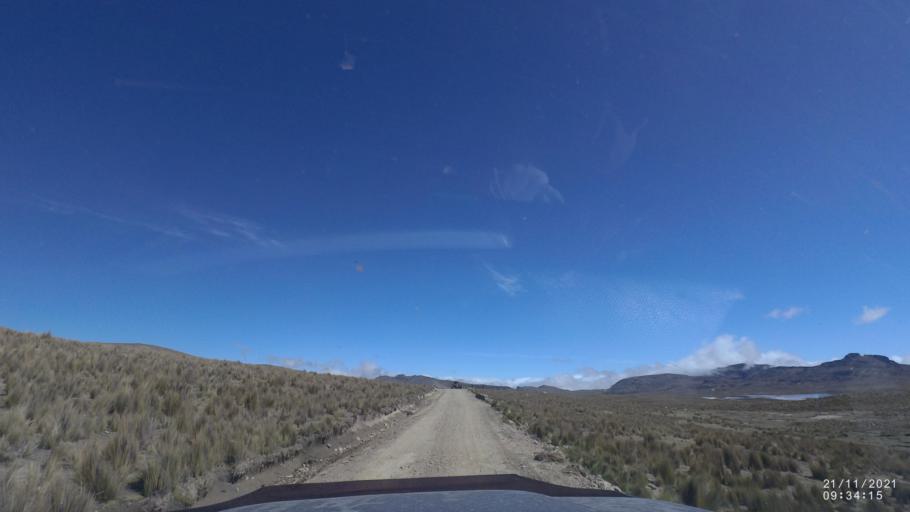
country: BO
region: Cochabamba
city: Cochabamba
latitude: -17.0577
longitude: -66.2596
